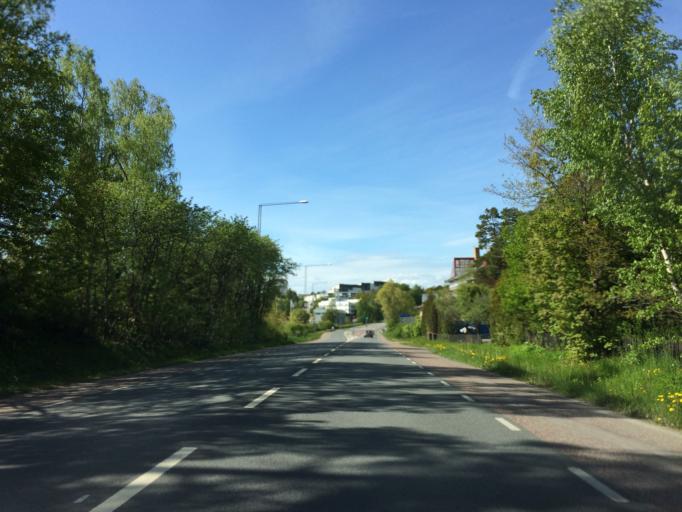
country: SE
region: Stockholm
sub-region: Sollentuna Kommun
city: Sollentuna
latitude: 59.4248
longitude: 18.0004
